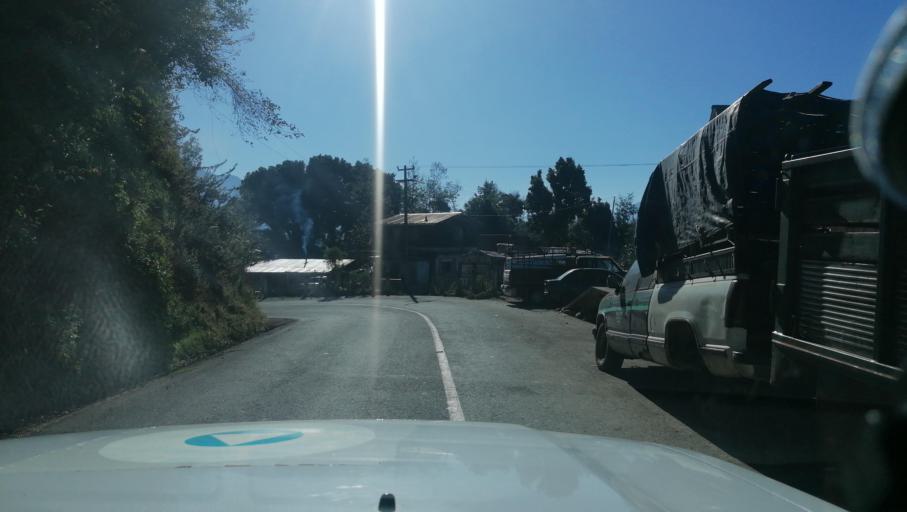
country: MX
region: Chiapas
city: Motozintla de Mendoza
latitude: 15.2512
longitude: -92.2230
